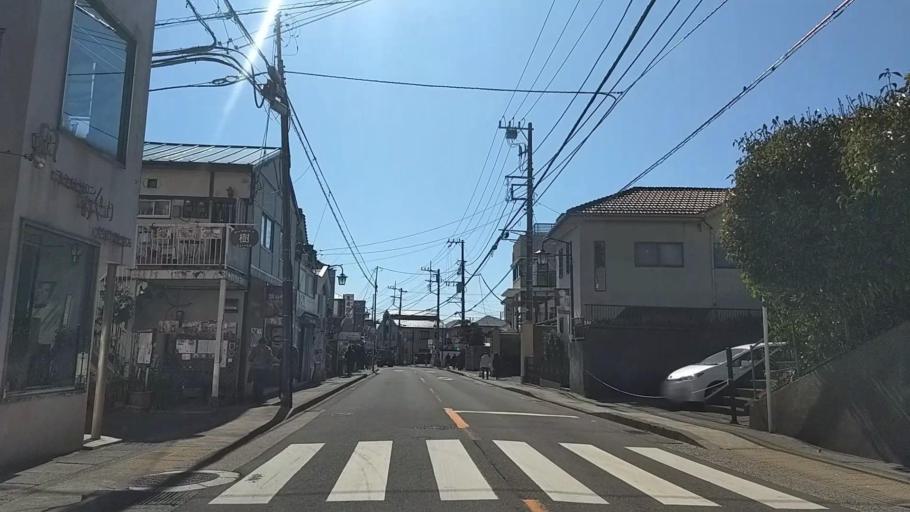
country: JP
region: Kanagawa
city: Kamakura
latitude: 35.3151
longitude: 139.5351
